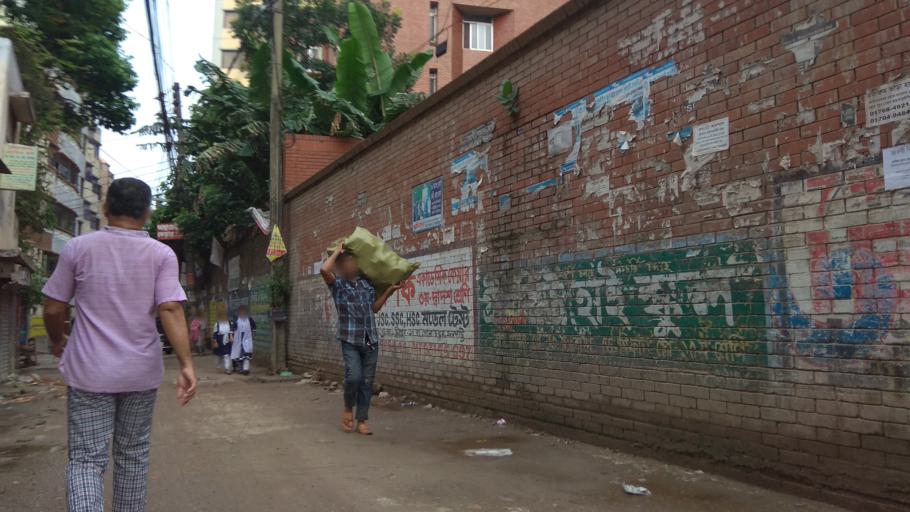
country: BD
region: Dhaka
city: Azimpur
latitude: 23.8022
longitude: 90.3614
